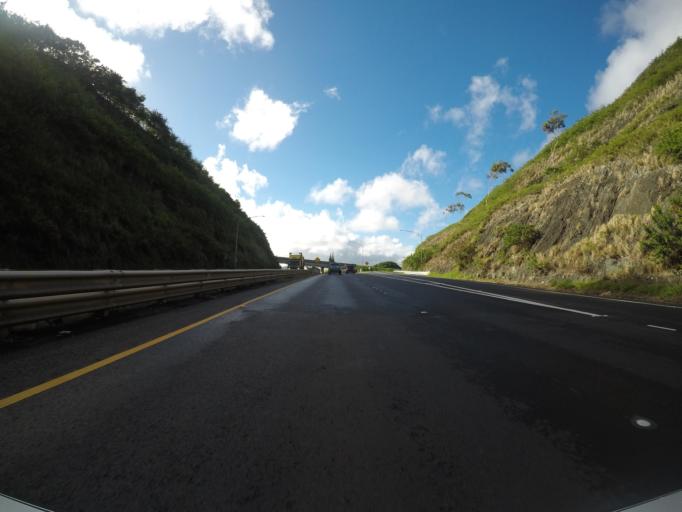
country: US
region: Hawaii
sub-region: Honolulu County
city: Kailua
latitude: 21.4075
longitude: -157.7675
